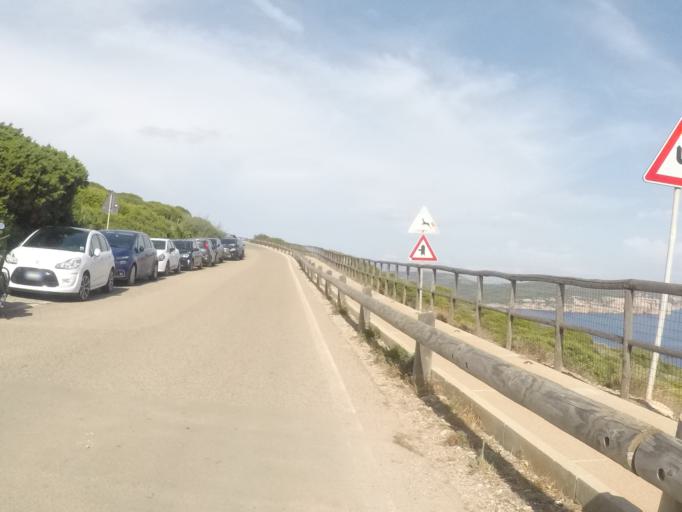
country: IT
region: Sardinia
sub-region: Provincia di Sassari
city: Alghero
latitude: 40.5635
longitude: 8.1635
